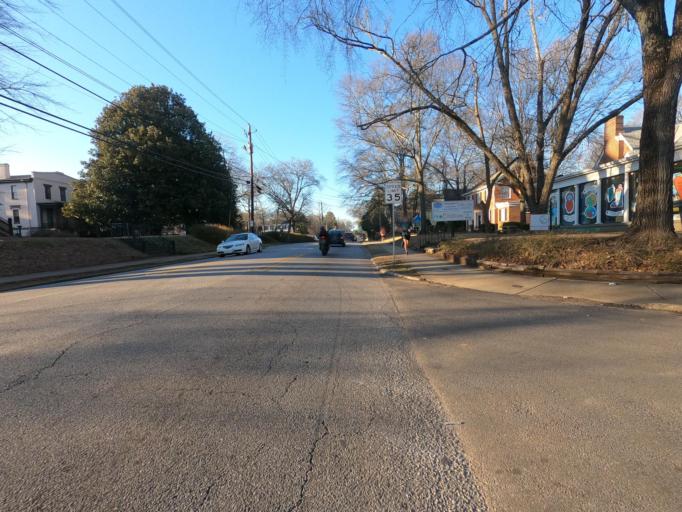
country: US
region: Georgia
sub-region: Clarke County
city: Athens
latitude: 33.9561
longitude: -83.3887
